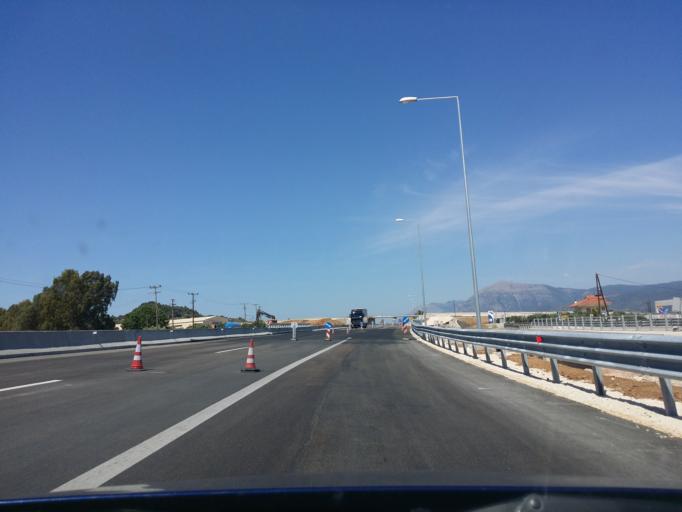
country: GR
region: West Greece
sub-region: Nomos Achaias
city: Ano Kastritsion
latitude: 38.3238
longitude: 21.8609
